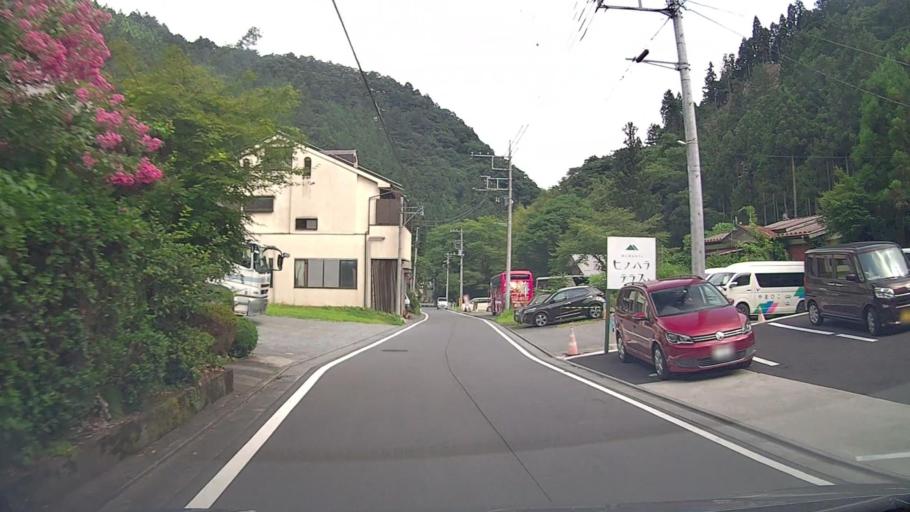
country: JP
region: Tokyo
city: Itsukaichi
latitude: 35.7463
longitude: 139.1222
